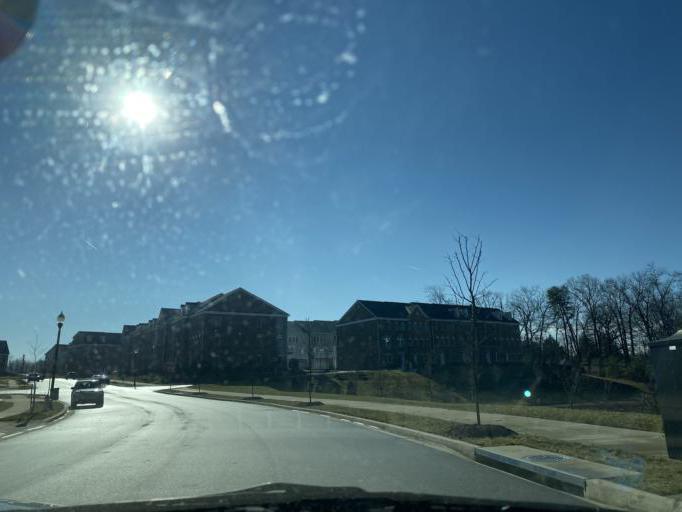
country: US
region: Maryland
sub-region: Prince George's County
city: West Laurel
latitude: 39.0891
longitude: -76.9187
